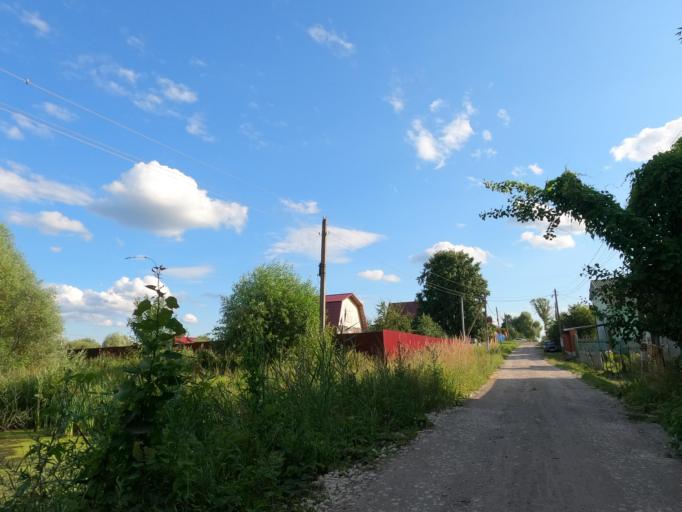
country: RU
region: Moskovskaya
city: Konobeyevo
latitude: 55.4127
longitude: 38.7200
